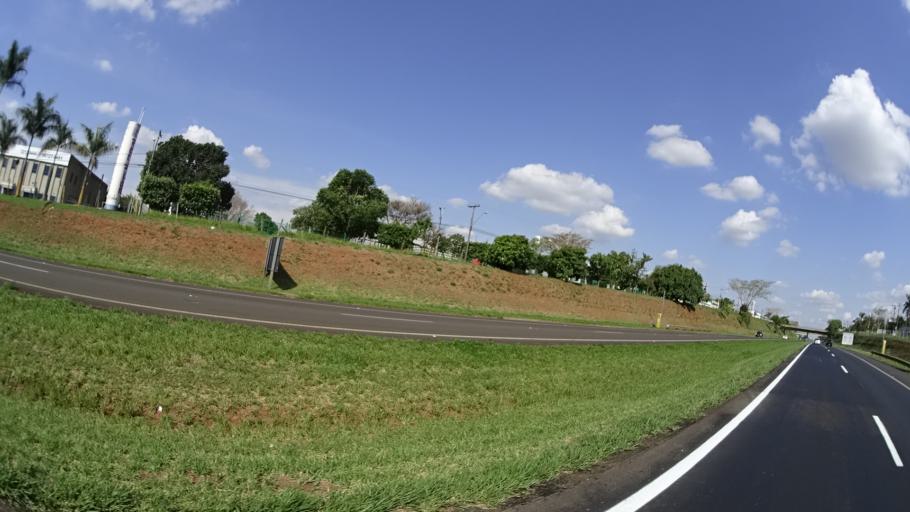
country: BR
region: Sao Paulo
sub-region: Sao Jose Do Rio Preto
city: Sao Jose do Rio Preto
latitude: -20.8473
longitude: -49.3470
